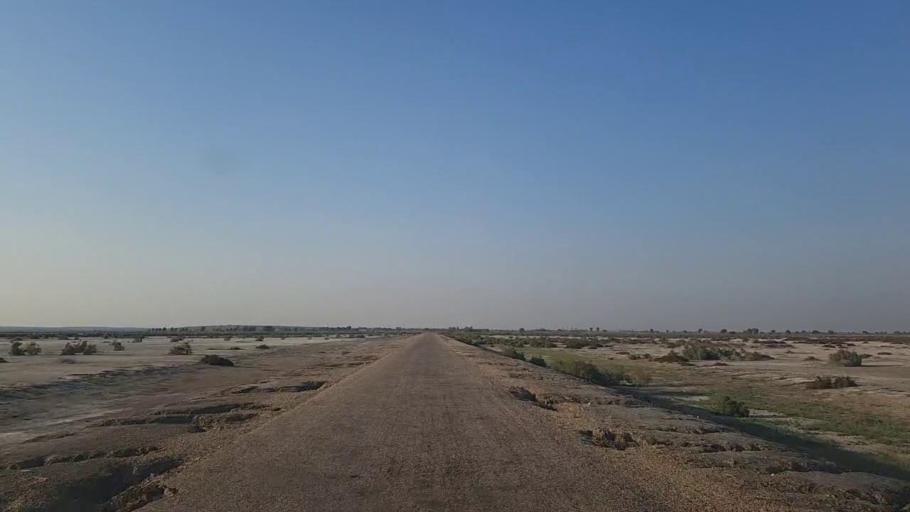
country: PK
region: Sindh
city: Jam Sahib
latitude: 26.3221
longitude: 68.6687
